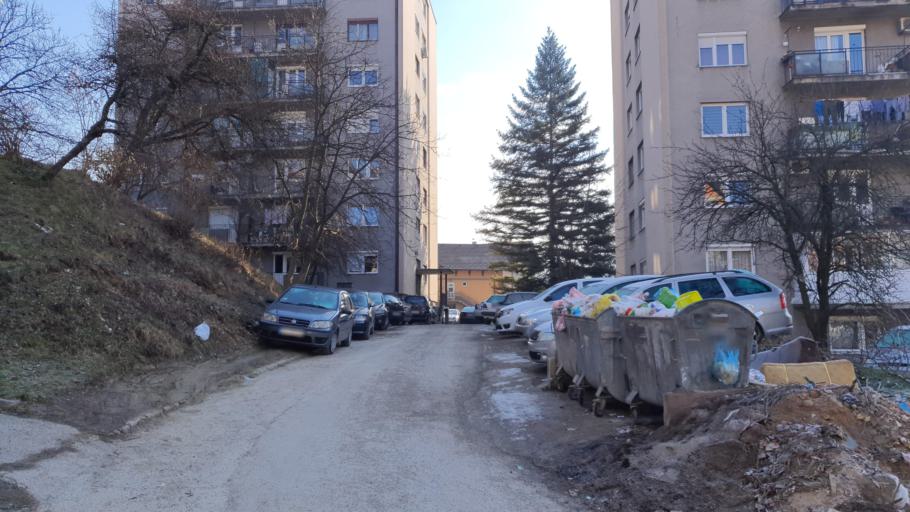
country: RS
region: Central Serbia
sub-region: Zlatiborski Okrug
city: Uzice
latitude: 43.8555
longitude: 19.8530
